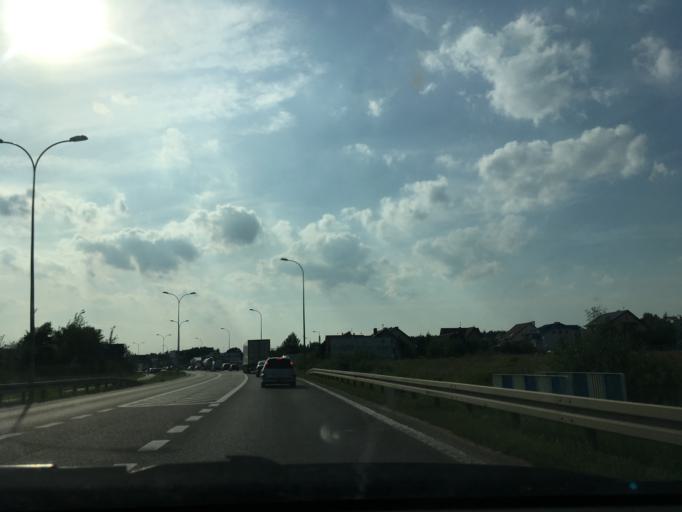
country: PL
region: Podlasie
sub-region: Bialystok
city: Bialystok
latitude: 53.1260
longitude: 23.2358
